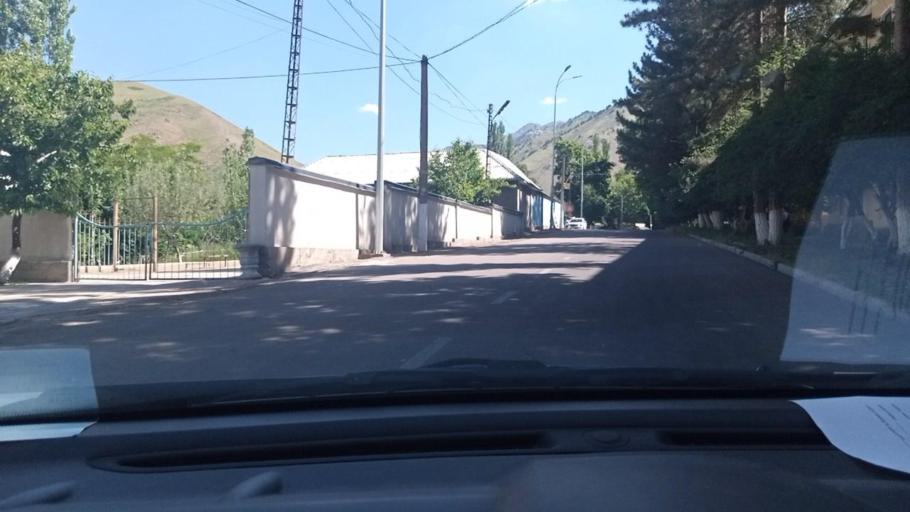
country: UZ
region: Toshkent
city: Yangiobod
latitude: 41.1171
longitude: 70.0904
